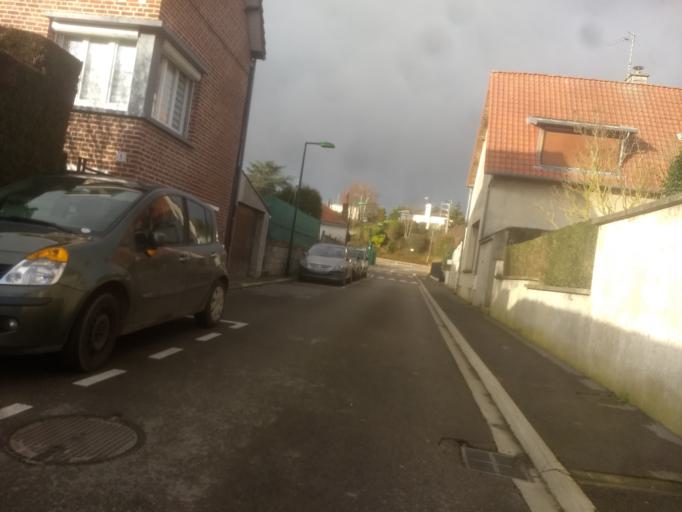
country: FR
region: Nord-Pas-de-Calais
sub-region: Departement du Pas-de-Calais
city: Saint-Laurent-Blangy
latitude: 50.3031
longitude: 2.8074
